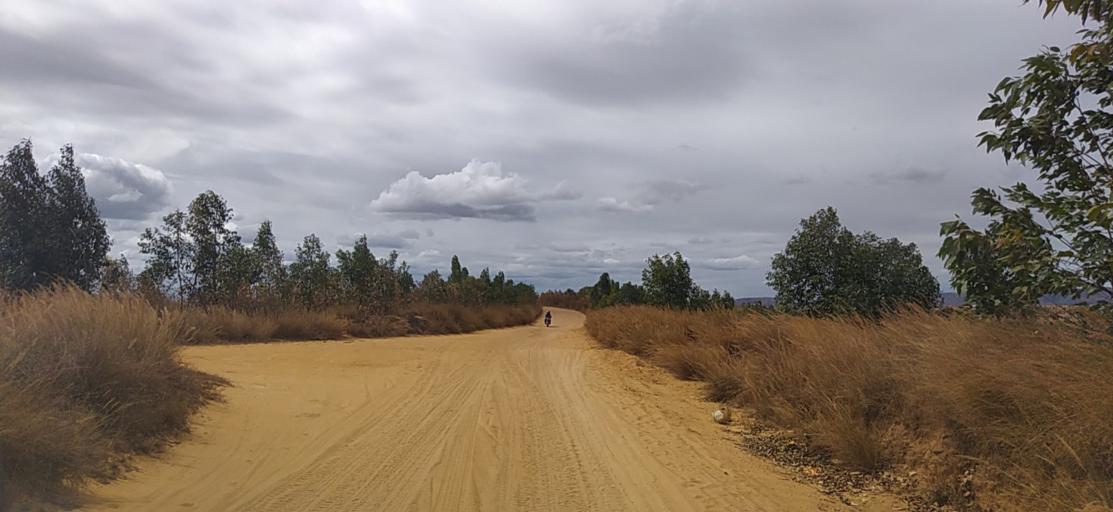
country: MG
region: Alaotra Mangoro
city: Ambatondrazaka
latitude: -17.9452
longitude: 48.2484
